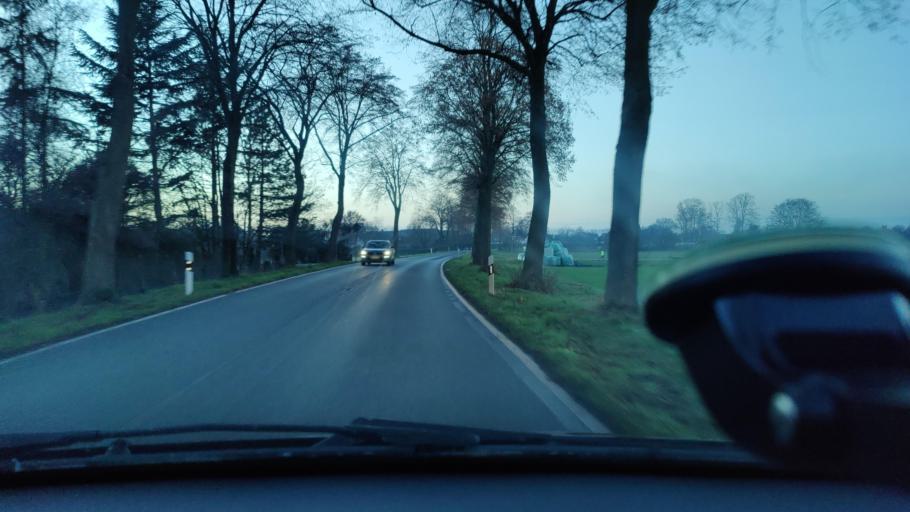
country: DE
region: North Rhine-Westphalia
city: Rheinberg
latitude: 51.5740
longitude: 6.6326
